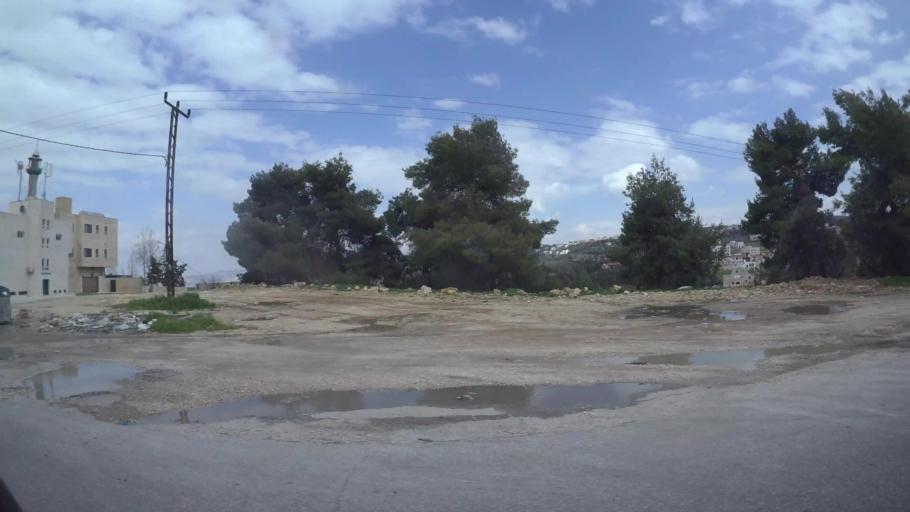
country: JO
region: Balqa
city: As Salt
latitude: 32.0328
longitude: 35.7937
